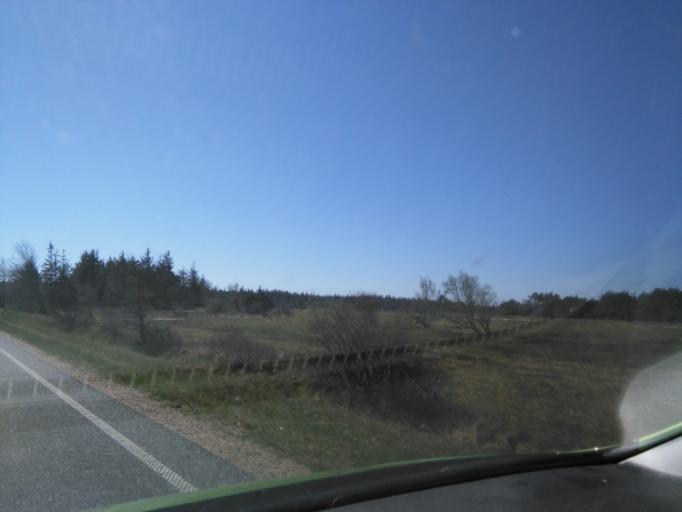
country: DK
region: South Denmark
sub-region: Varde Kommune
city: Oksbol
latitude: 55.6098
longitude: 8.2282
